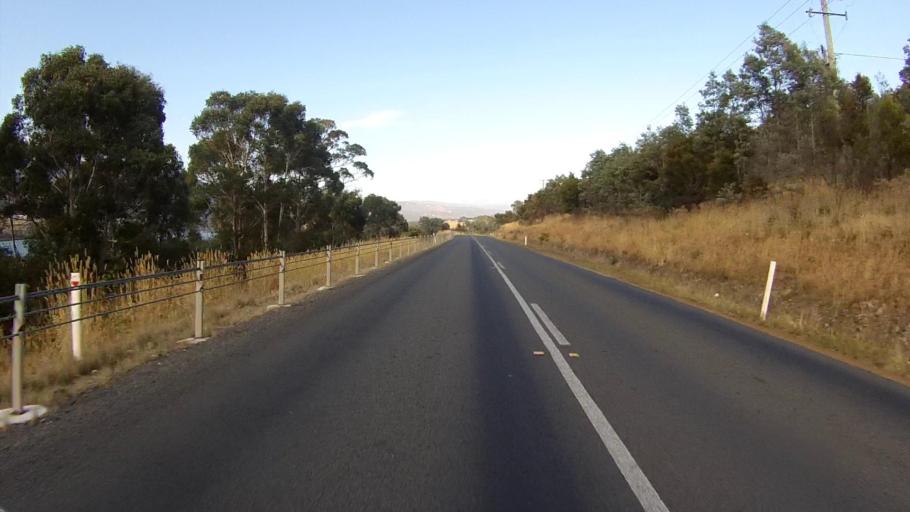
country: AU
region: Tasmania
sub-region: Glenorchy
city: Granton
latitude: -42.7532
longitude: 147.1474
